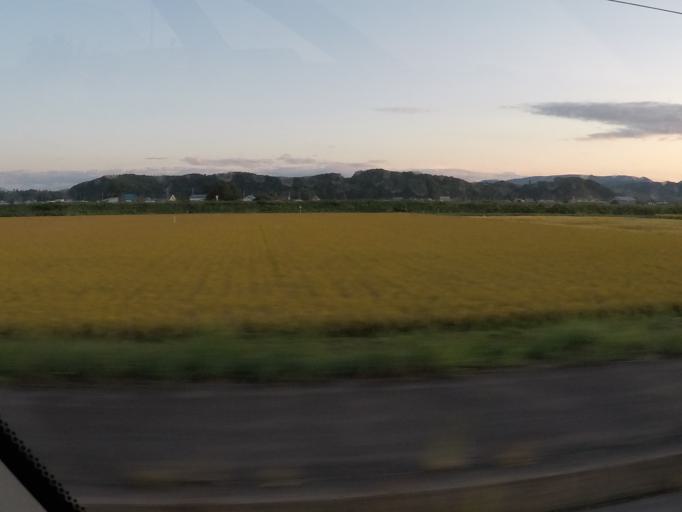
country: JP
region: Hokkaido
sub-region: Asahikawa-shi
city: Asahikawa
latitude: 43.6653
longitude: 142.4199
